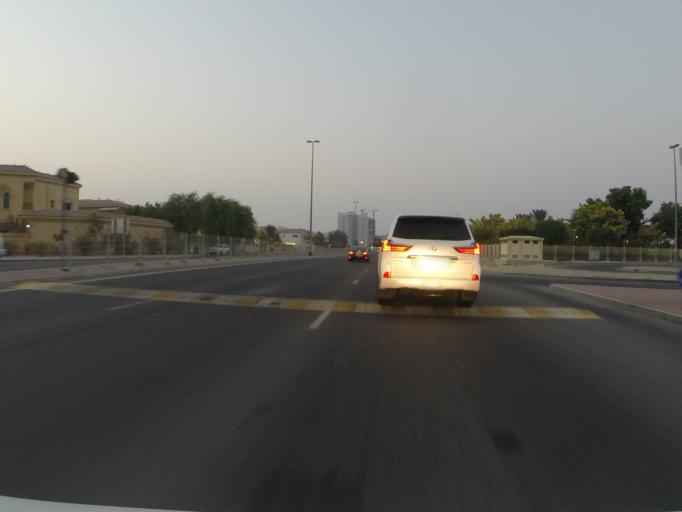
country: AE
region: Dubai
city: Dubai
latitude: 25.0997
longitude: 55.1998
